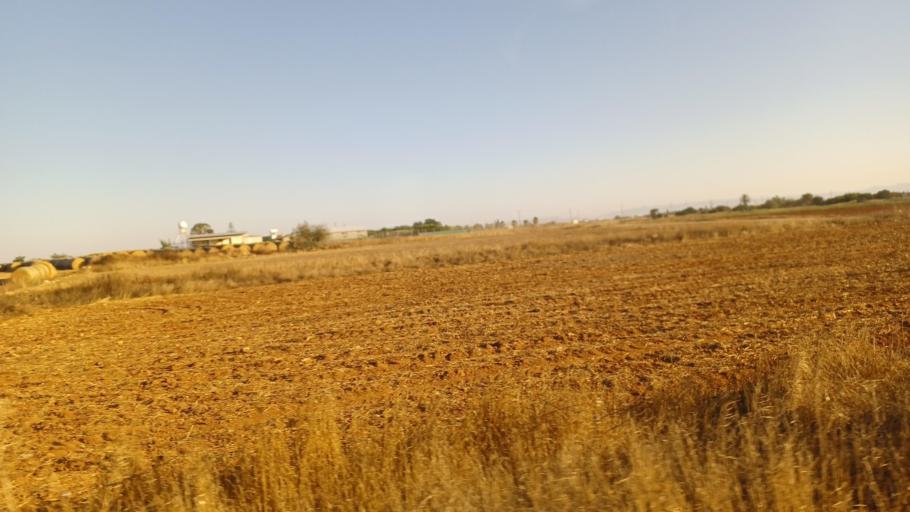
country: CY
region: Ammochostos
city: Avgorou
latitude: 35.0069
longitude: 33.8362
